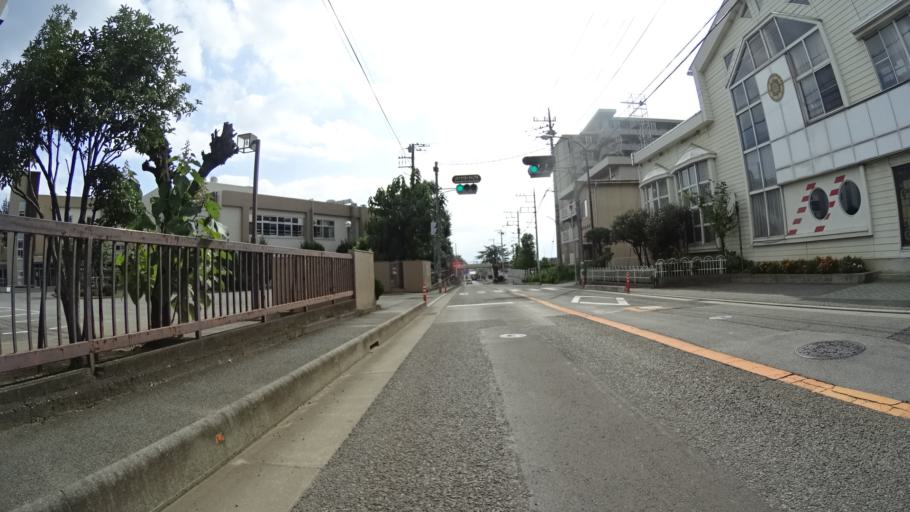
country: JP
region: Yamanashi
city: Kofu-shi
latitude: 35.6804
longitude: 138.5674
